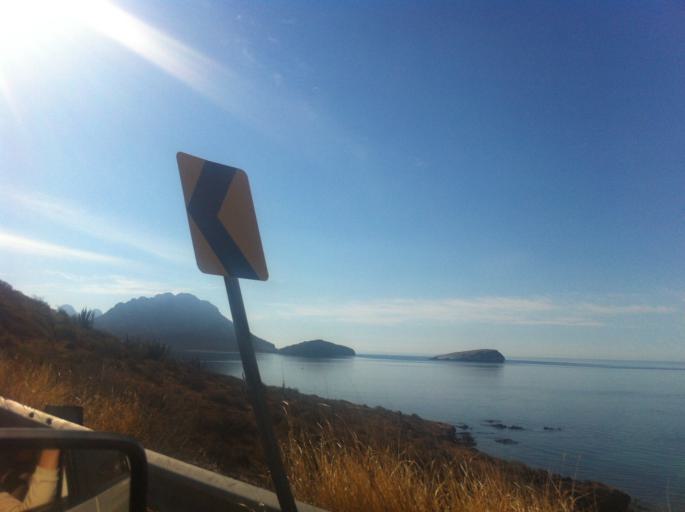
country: MX
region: Sonora
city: Heroica Guaymas
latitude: 27.9284
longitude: -110.9652
